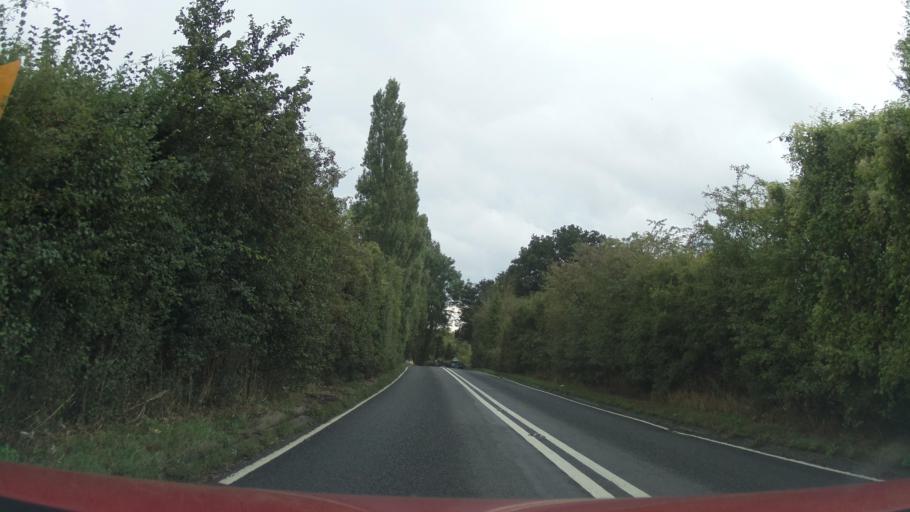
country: GB
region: England
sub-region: Worcestershire
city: Droitwich
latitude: 52.3214
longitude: -2.1763
